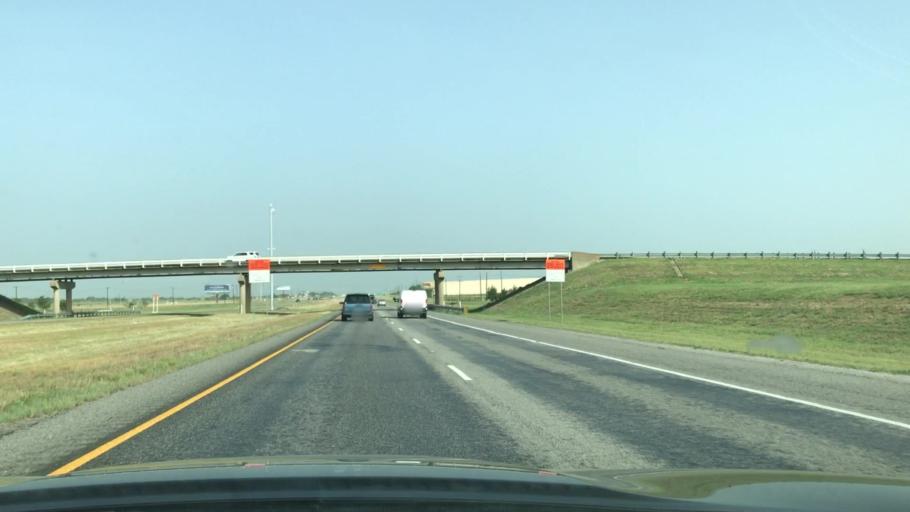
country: US
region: Texas
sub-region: Kaufman County
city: Terrell
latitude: 32.7204
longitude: -96.3184
